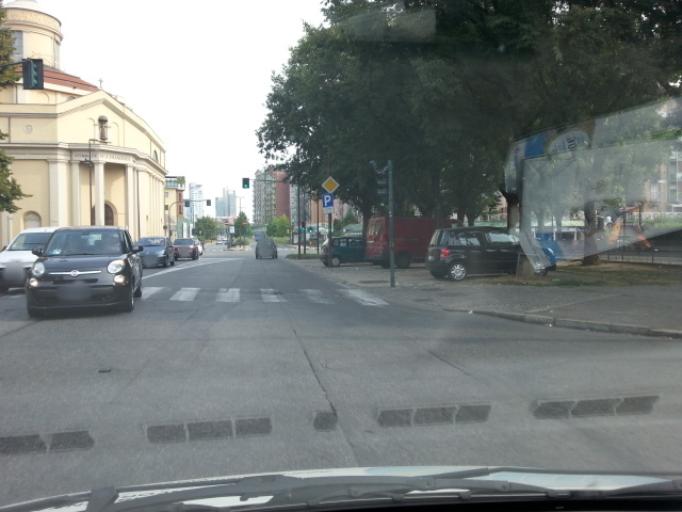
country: IT
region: Piedmont
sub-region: Provincia di Torino
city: Turin
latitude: 45.0845
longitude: 7.6681
